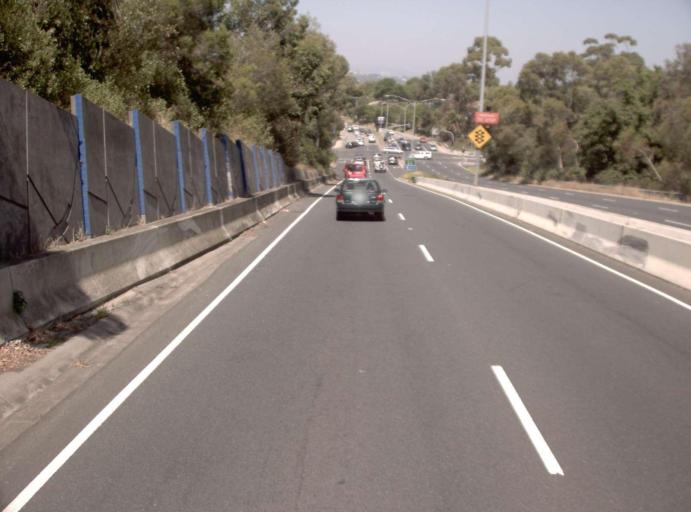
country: AU
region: Victoria
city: Rosanna
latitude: -37.7573
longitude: 145.0571
